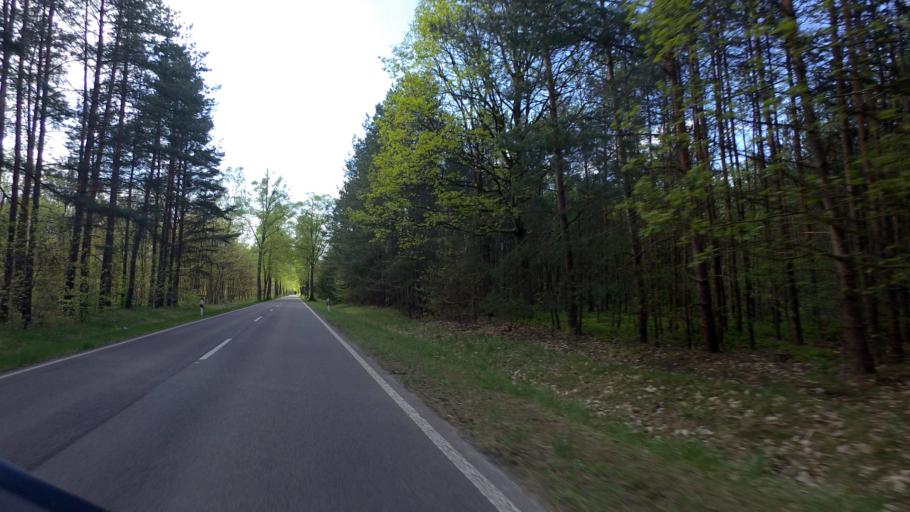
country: DE
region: Brandenburg
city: Friedrichswalde
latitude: 53.0019
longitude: 13.5887
